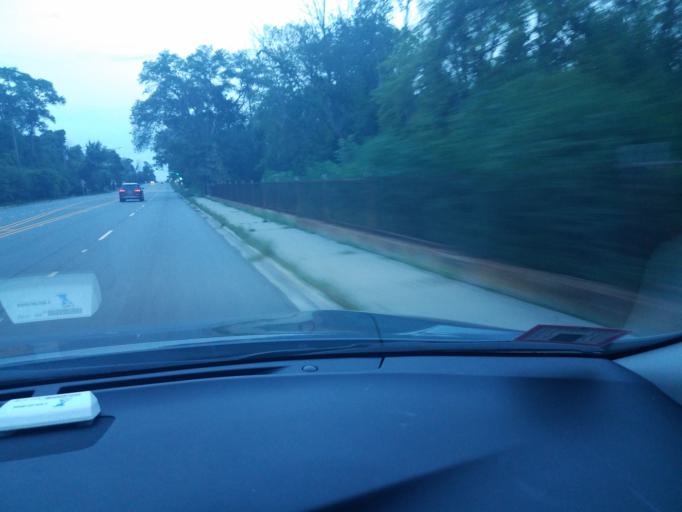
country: US
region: Illinois
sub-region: Cook County
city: Northbrook
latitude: 42.1380
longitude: -87.8090
